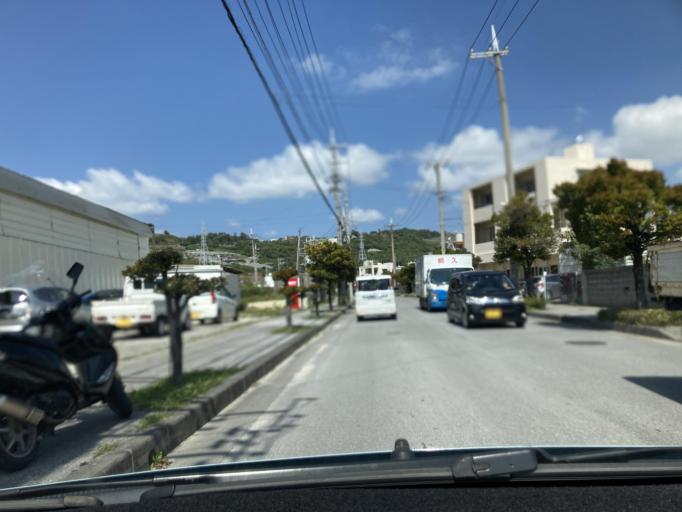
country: JP
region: Okinawa
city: Ginowan
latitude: 26.2610
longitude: 127.7912
